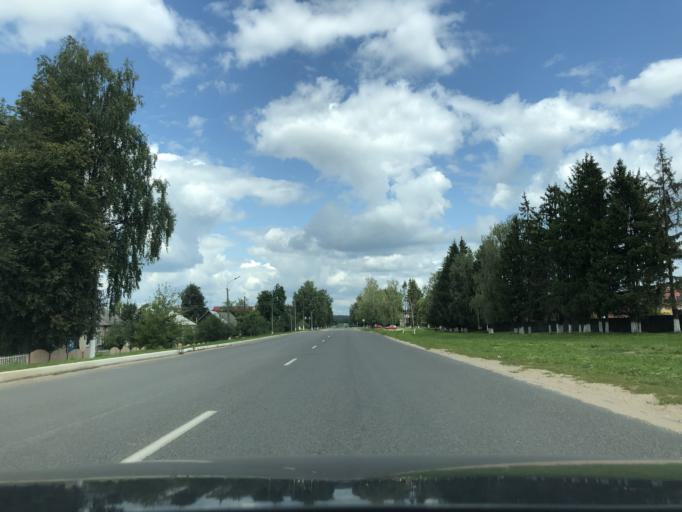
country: BY
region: Minsk
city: Lahoysk
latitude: 54.2132
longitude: 27.8517
